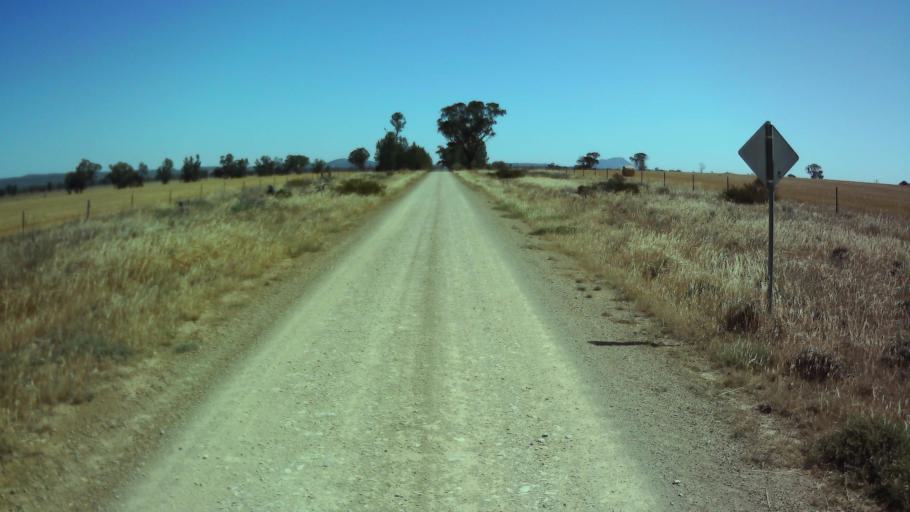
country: AU
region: New South Wales
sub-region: Weddin
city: Grenfell
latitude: -33.8775
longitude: 147.8738
